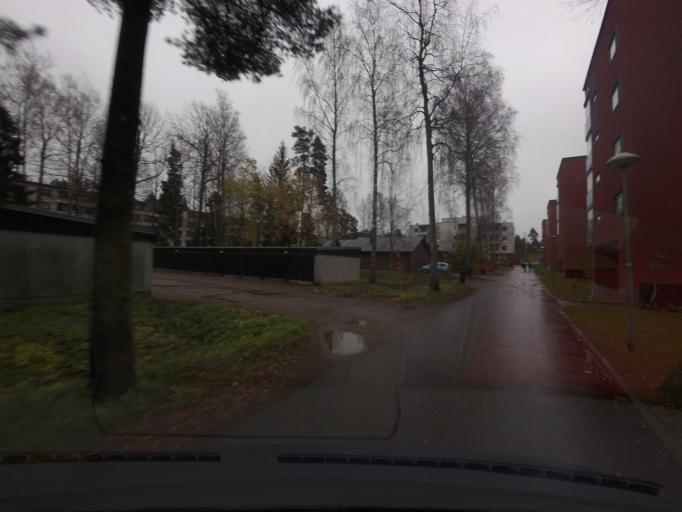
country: FI
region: Uusimaa
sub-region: Helsinki
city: Kilo
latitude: 60.2303
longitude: 24.7638
